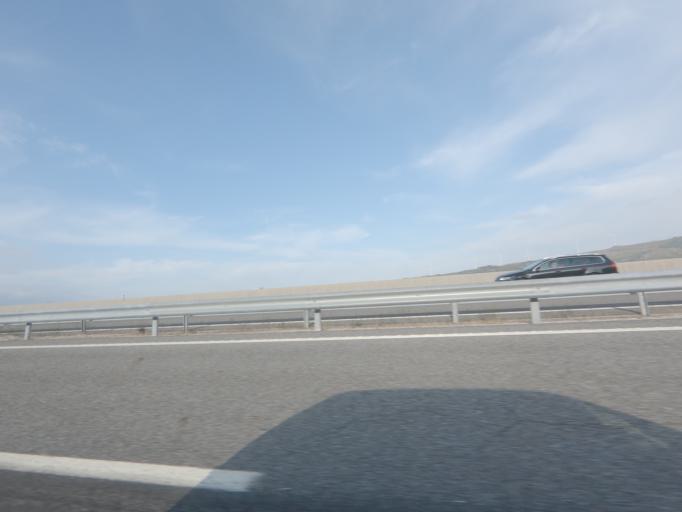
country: PT
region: Vila Real
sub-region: Vila Pouca de Aguiar
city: Vila Pouca de Aguiar
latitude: 41.4966
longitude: -7.6561
